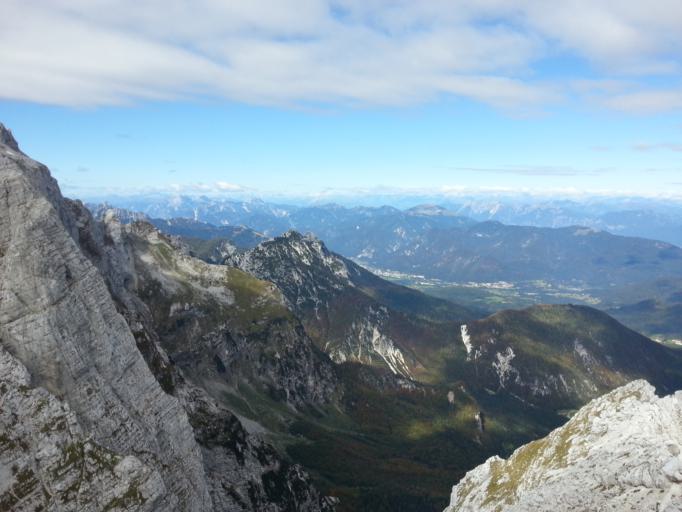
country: SI
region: Kranjska Gora
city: Kranjska Gora
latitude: 46.4395
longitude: 13.6852
